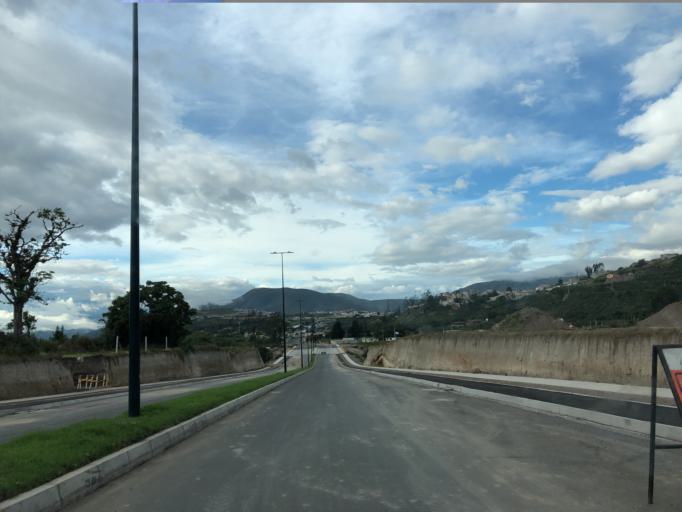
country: EC
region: Imbabura
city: Ibarra
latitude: 0.3424
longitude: -78.1527
